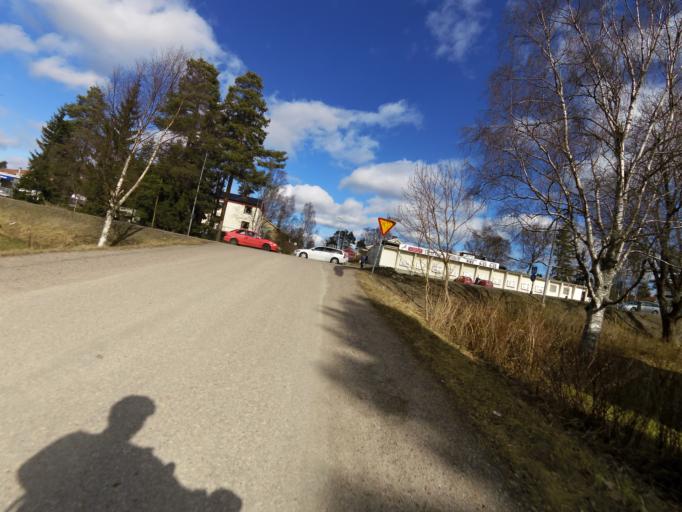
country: SE
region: Gaevleborg
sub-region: Hofors Kommun
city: Hofors
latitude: 60.5412
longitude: 16.2783
